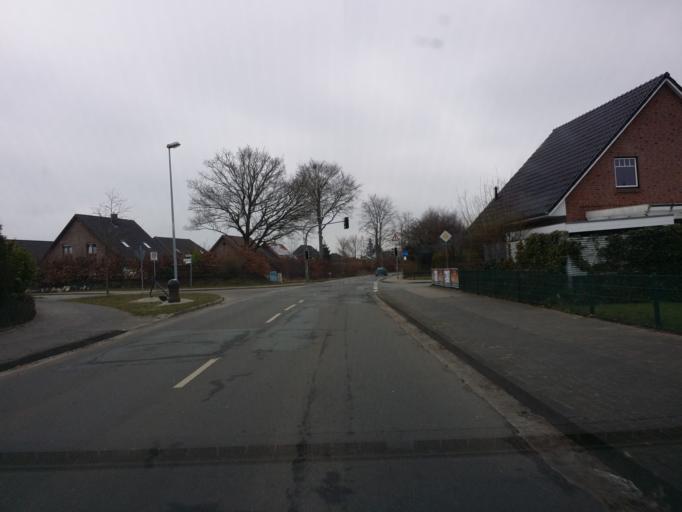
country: DE
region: Schleswig-Holstein
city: Schacht-Audorf
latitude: 54.3142
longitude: 9.7228
